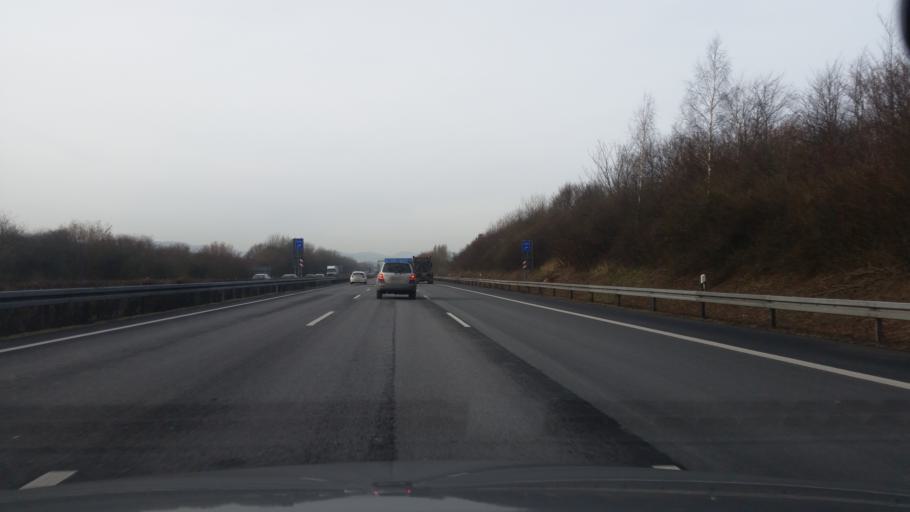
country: DE
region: Lower Saxony
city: Rehren
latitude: 52.2343
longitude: 9.2584
